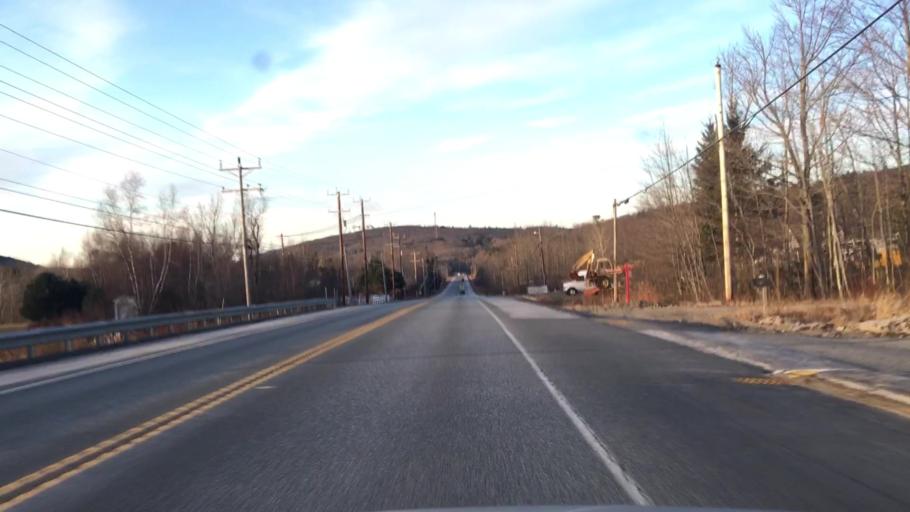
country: US
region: Maine
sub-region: Hancock County
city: Dedham
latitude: 44.7052
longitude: -68.5999
